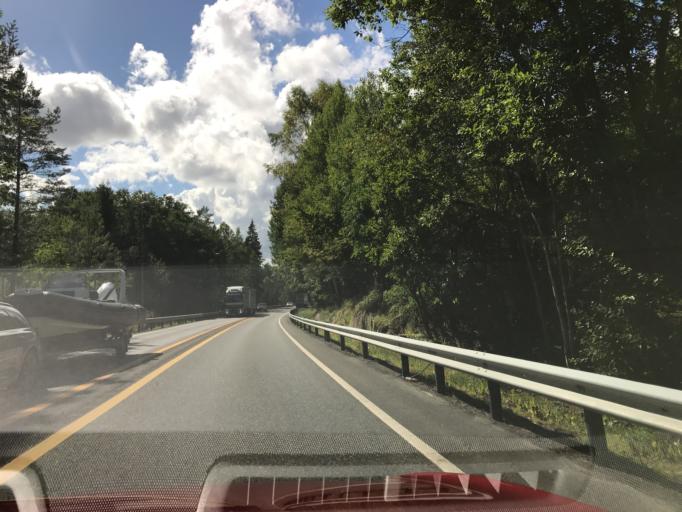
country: NO
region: Telemark
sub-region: Kragero
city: Kragero
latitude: 58.9611
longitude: 9.4579
